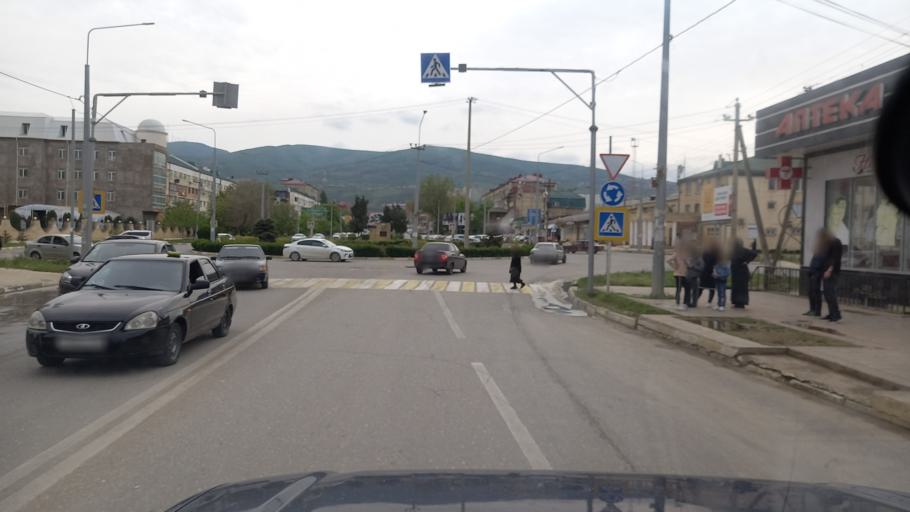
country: RU
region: Dagestan
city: Derbent
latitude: 42.0702
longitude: 48.2956
